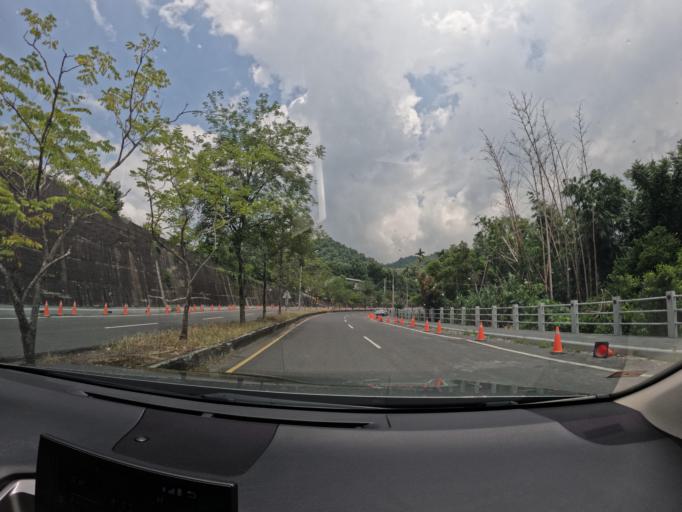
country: TW
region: Taiwan
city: Lugu
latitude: 23.8017
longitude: 120.7881
